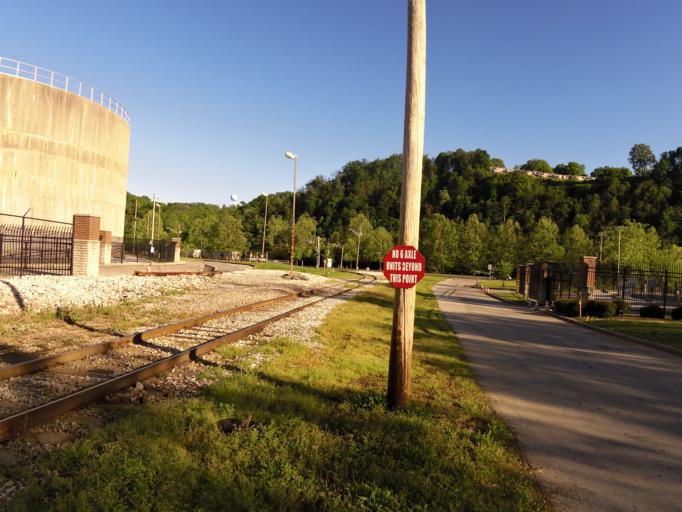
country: US
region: Tennessee
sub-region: Knox County
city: Knoxville
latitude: 35.9443
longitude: -83.9352
